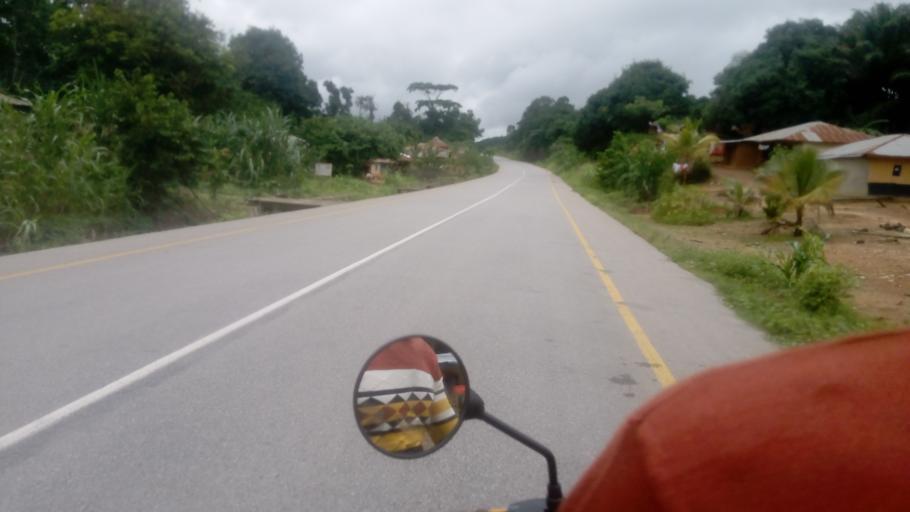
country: SL
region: Northern Province
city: Masaka
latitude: 8.6439
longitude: -11.7369
